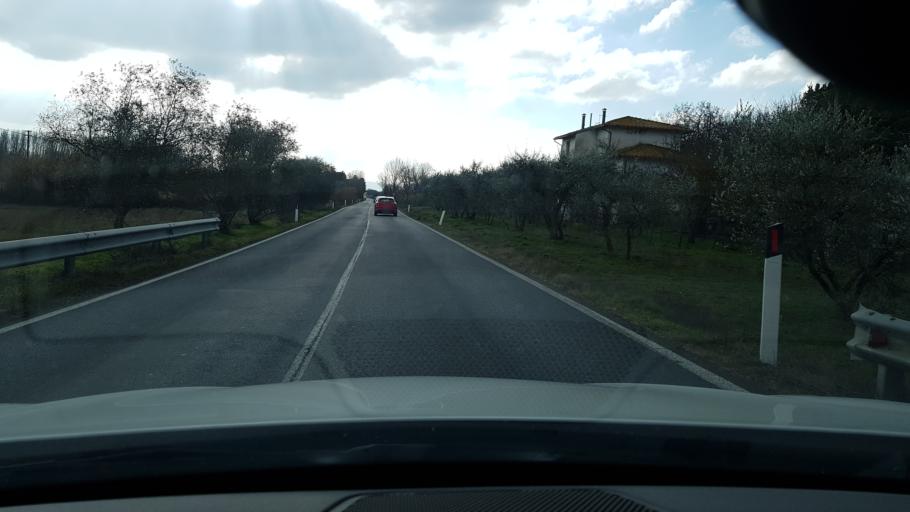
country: IT
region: Umbria
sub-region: Provincia di Perugia
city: Castiglione del Lago
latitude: 43.1602
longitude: 12.0165
